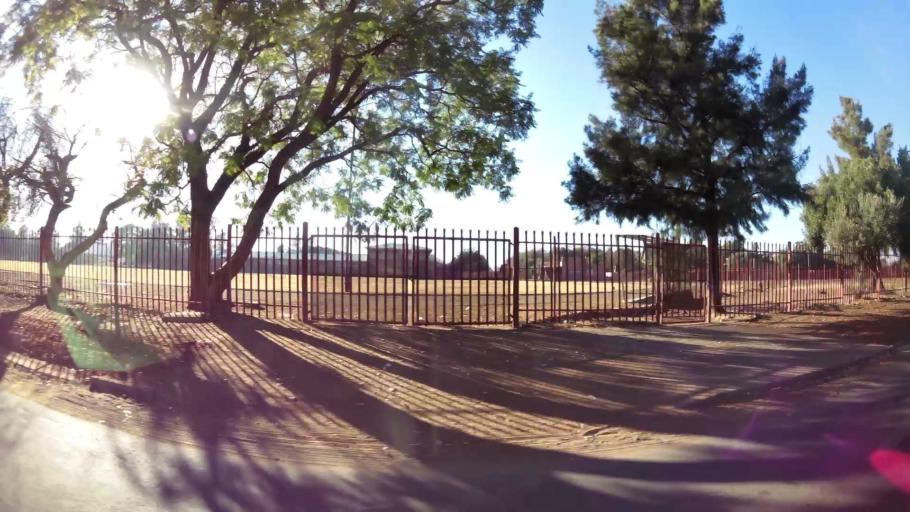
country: ZA
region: Northern Cape
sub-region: Frances Baard District Municipality
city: Kimberley
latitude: -28.7375
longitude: 24.7353
